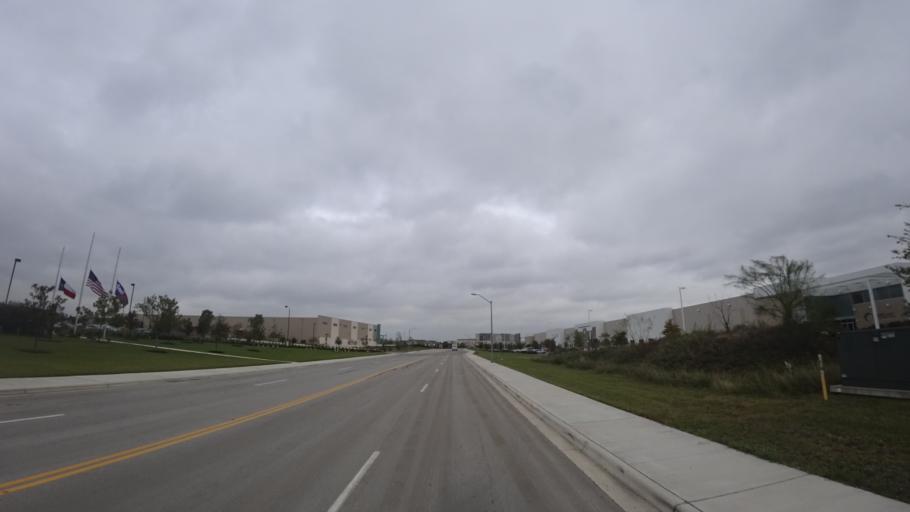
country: US
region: Texas
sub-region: Travis County
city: Pflugerville
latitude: 30.4184
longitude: -97.5906
